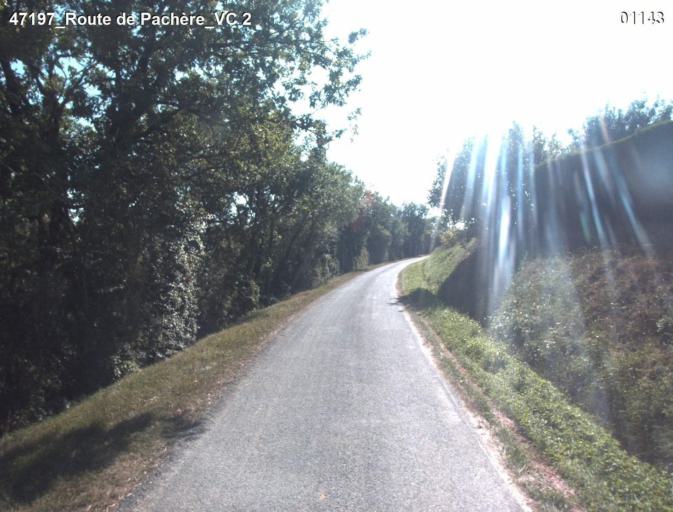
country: FR
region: Aquitaine
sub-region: Departement du Lot-et-Garonne
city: Laplume
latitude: 44.0911
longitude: 0.4596
